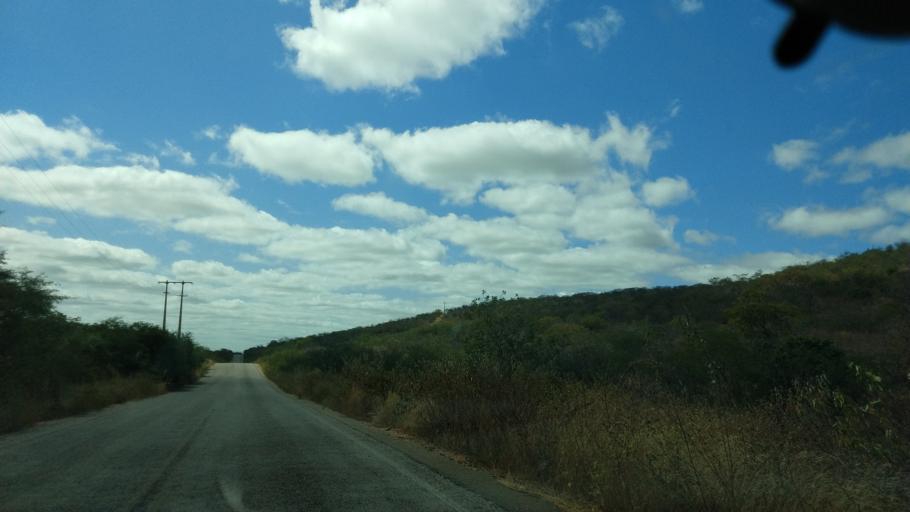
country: BR
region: Rio Grande do Norte
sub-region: Currais Novos
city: Currais Novos
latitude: -6.2619
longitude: -36.5804
